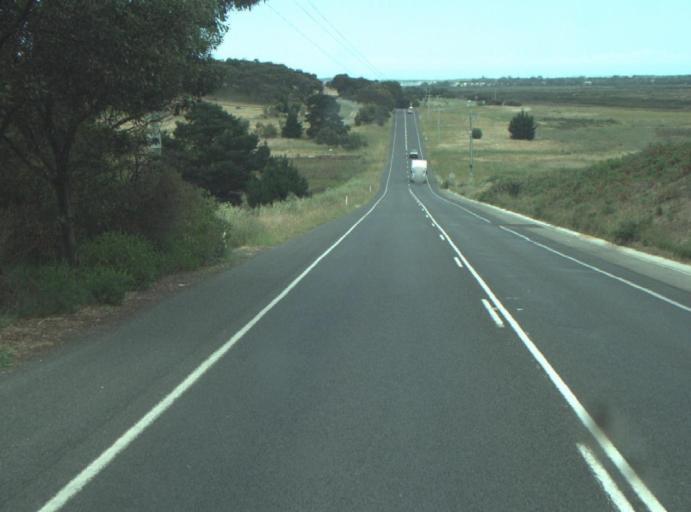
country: AU
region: Victoria
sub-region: Greater Geelong
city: Leopold
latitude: -38.2449
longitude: 144.5052
